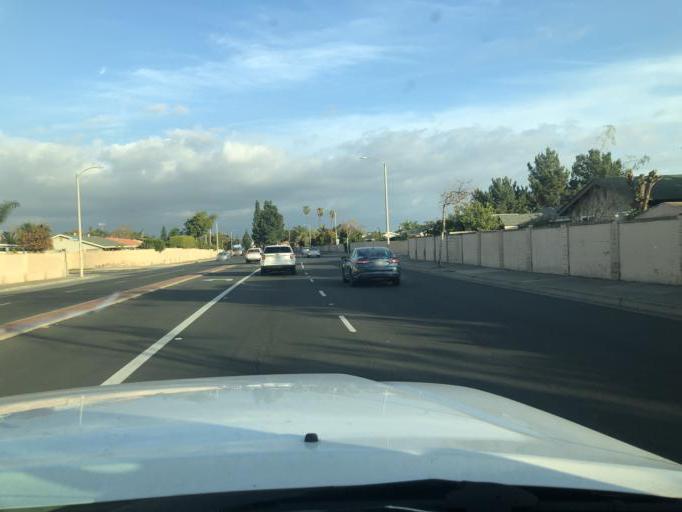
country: US
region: California
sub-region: Orange County
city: Santa Ana
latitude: 33.7271
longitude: -117.8620
